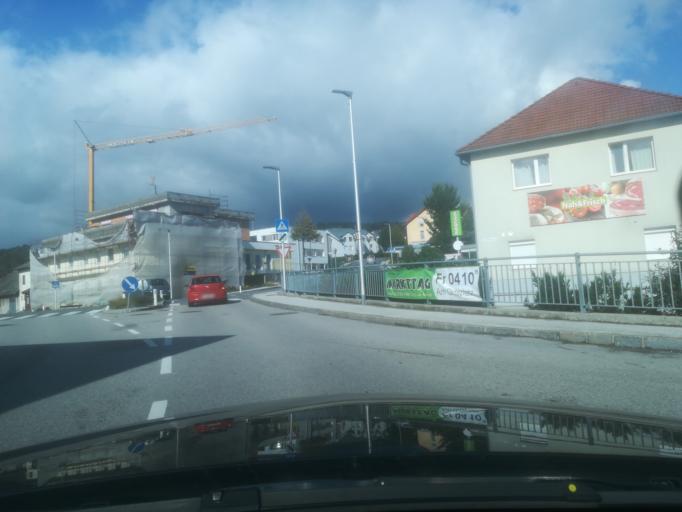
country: AT
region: Upper Austria
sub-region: Politischer Bezirk Urfahr-Umgebung
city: Eidenberg
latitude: 48.3598
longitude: 14.2579
